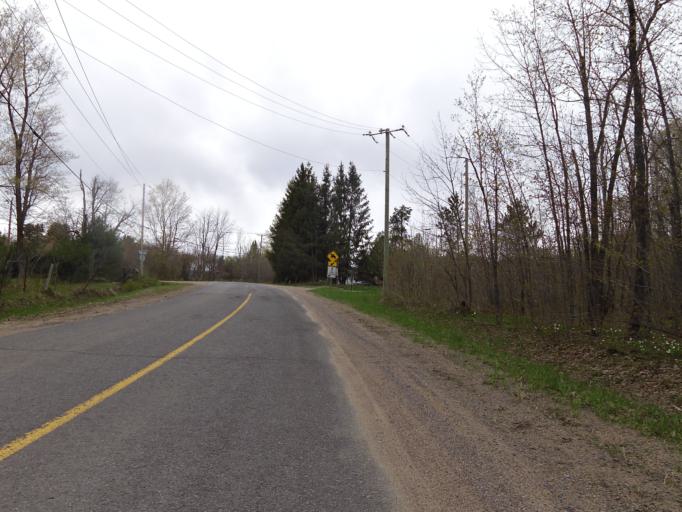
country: CA
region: Quebec
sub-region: Laurentides
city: Brownsburg-Chatham
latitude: 45.6117
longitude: -74.4791
